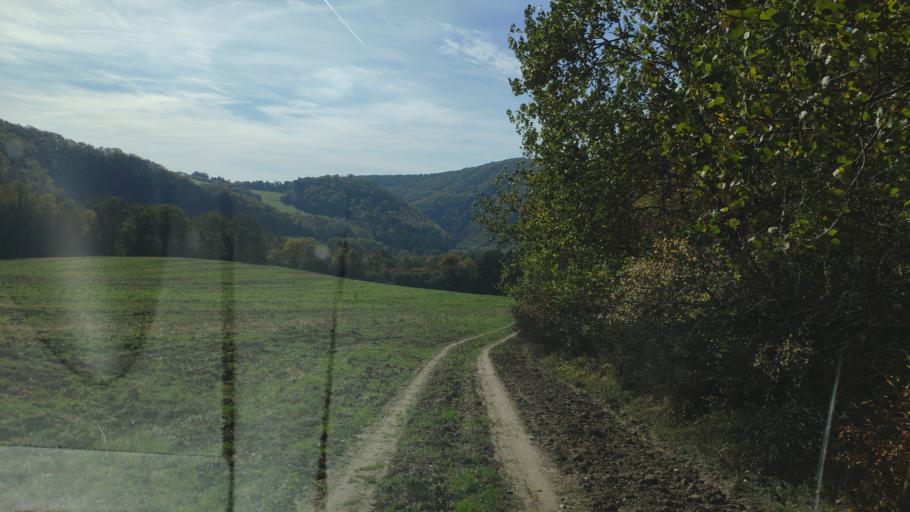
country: SK
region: Presovsky
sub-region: Okres Presov
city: Presov
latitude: 48.8825
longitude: 21.2288
